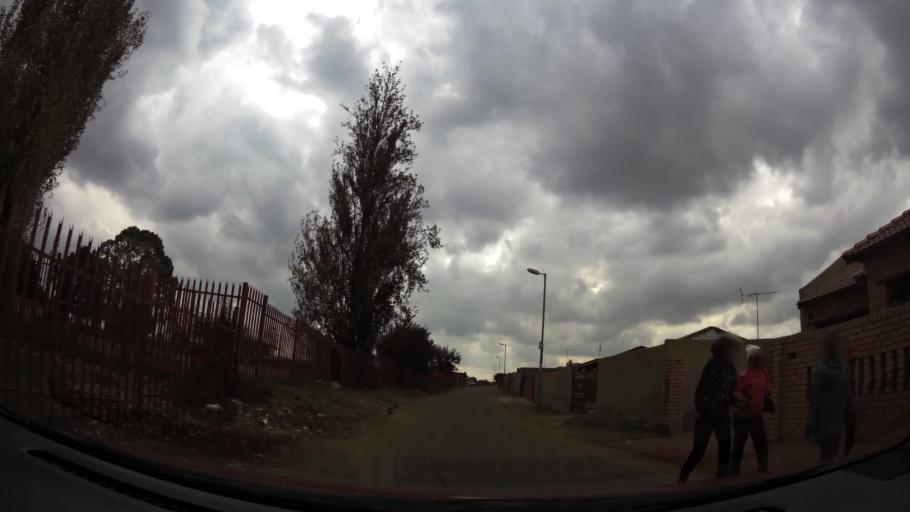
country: ZA
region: Gauteng
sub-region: City of Johannesburg Metropolitan Municipality
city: Soweto
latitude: -26.2581
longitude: 27.8418
